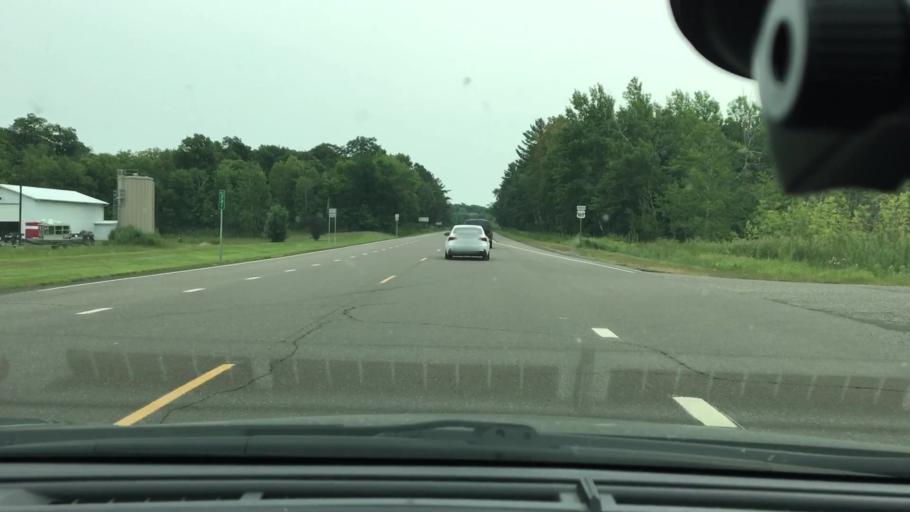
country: US
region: Minnesota
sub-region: Mille Lacs County
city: Vineland
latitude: 46.1454
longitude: -93.7242
